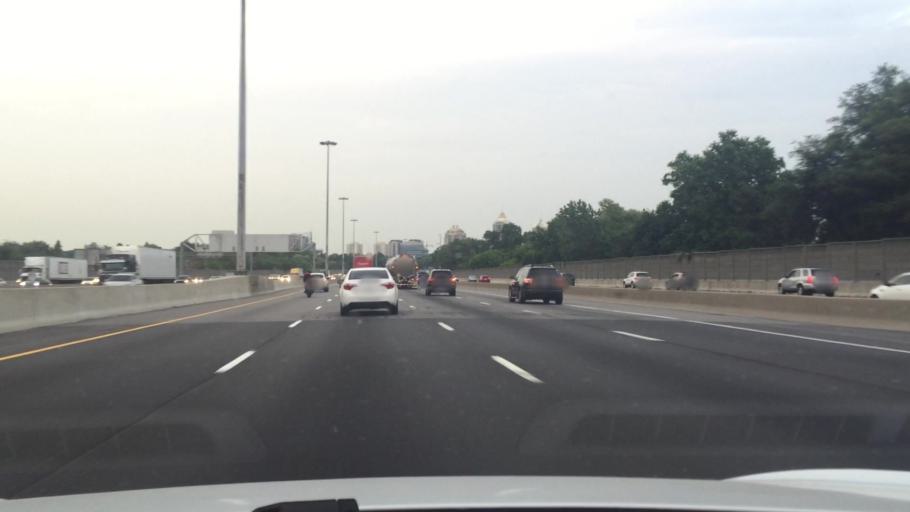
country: CA
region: Ontario
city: Willowdale
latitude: 43.7559
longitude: -79.4021
